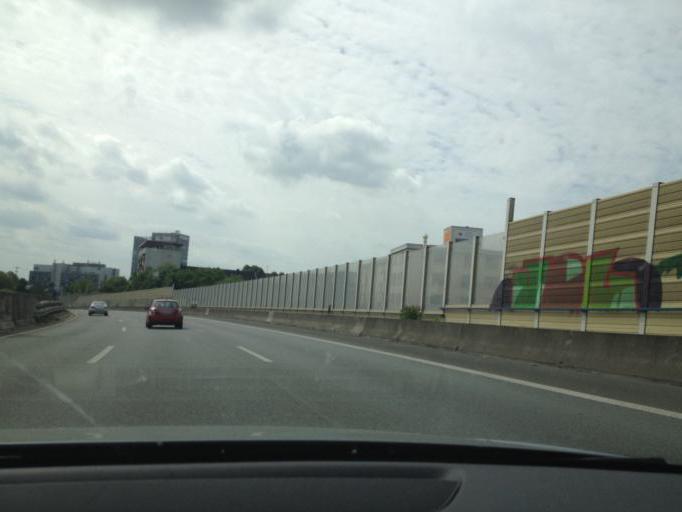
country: DE
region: North Rhine-Westphalia
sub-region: Regierungsbezirk Dusseldorf
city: Duisburg
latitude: 51.4383
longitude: 6.7751
